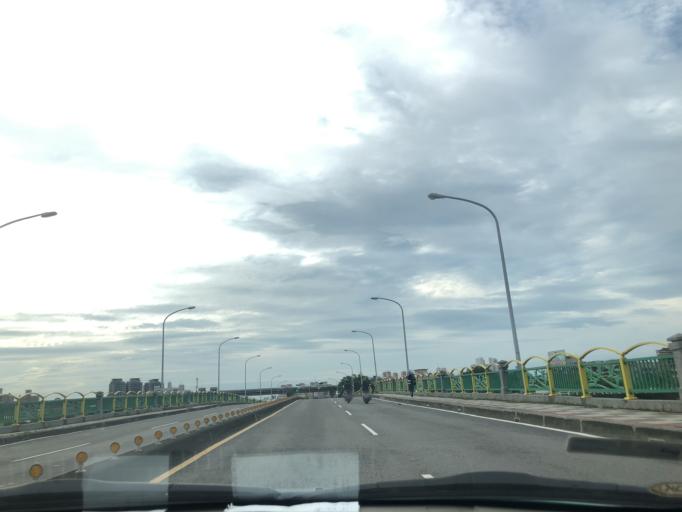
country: TW
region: Taiwan
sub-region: Taichung City
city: Taichung
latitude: 24.0974
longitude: 120.6951
